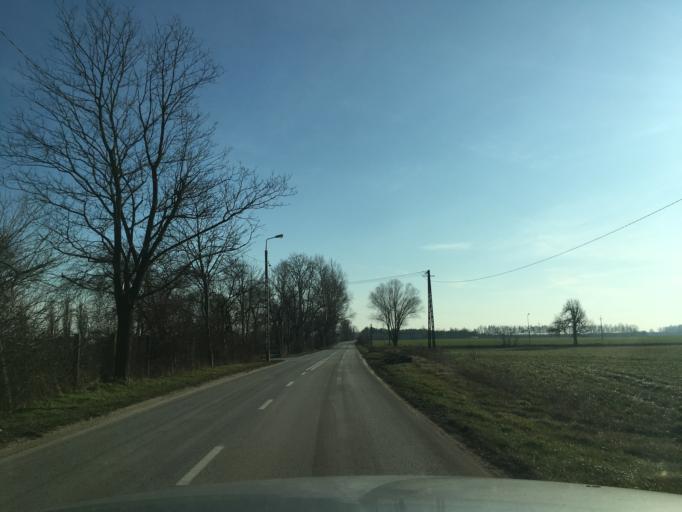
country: PL
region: Masovian Voivodeship
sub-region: Powiat pruszkowski
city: Nadarzyn
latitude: 52.0544
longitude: 20.8248
